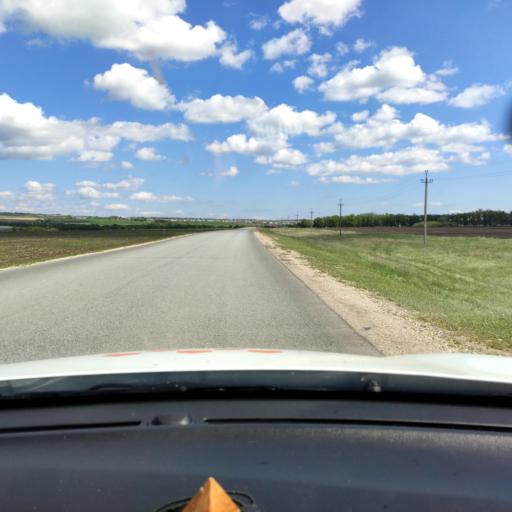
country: RU
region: Tatarstan
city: Kuybyshevskiy Zaton
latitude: 55.1675
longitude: 49.2088
